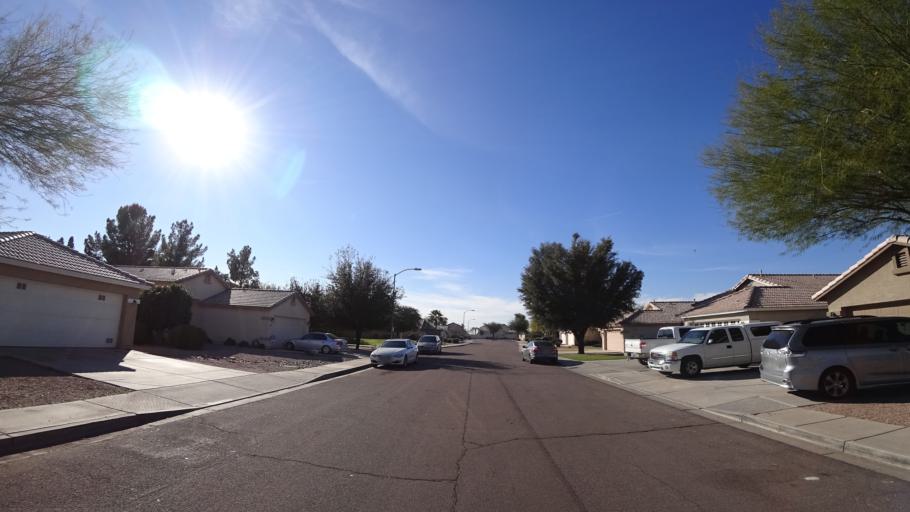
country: US
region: Arizona
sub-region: Maricopa County
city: Glendale
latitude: 33.5220
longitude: -112.2276
